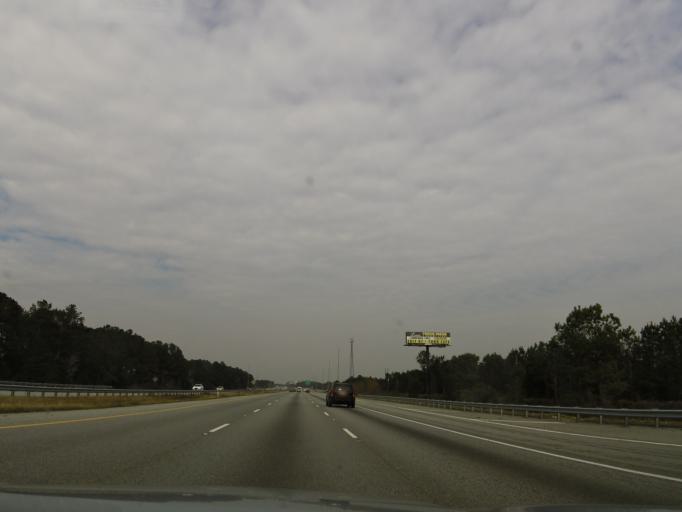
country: US
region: Georgia
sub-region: Liberty County
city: Midway
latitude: 31.6459
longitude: -81.3987
